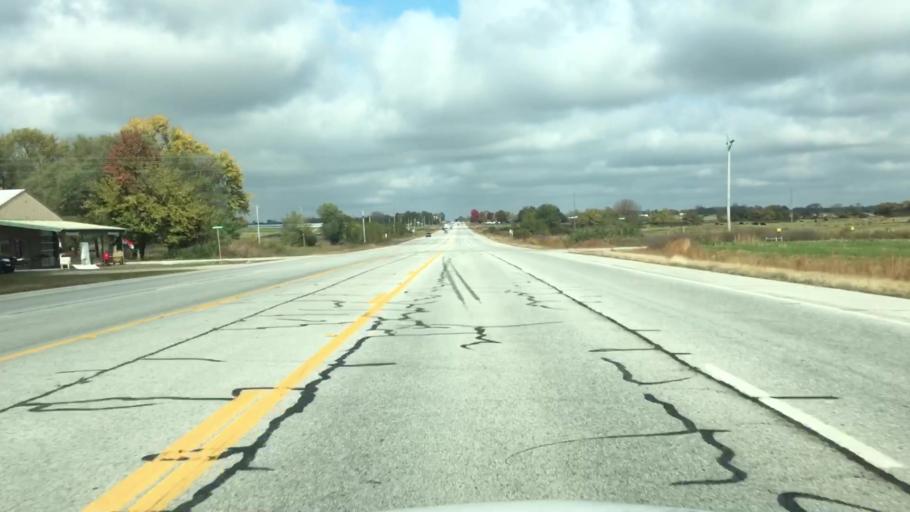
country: US
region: Arkansas
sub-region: Benton County
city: Siloam Springs
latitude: 36.2090
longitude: -94.4957
